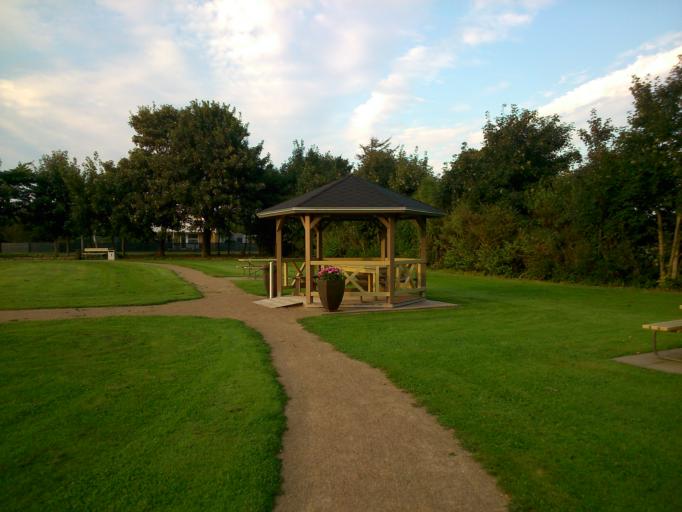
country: DK
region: Central Jutland
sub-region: Ringkobing-Skjern Kommune
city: Tarm
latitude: 55.9557
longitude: 8.6562
